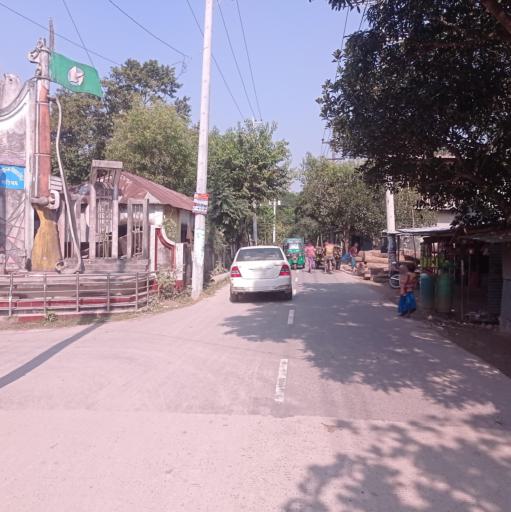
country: BD
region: Dhaka
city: Narsingdi
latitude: 24.0694
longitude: 90.6922
